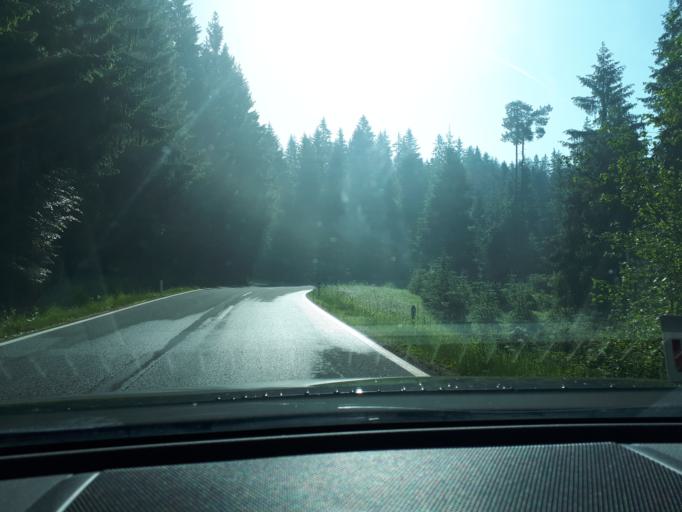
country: AT
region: Styria
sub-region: Politischer Bezirk Voitsberg
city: Pack
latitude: 46.9542
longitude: 14.9782
